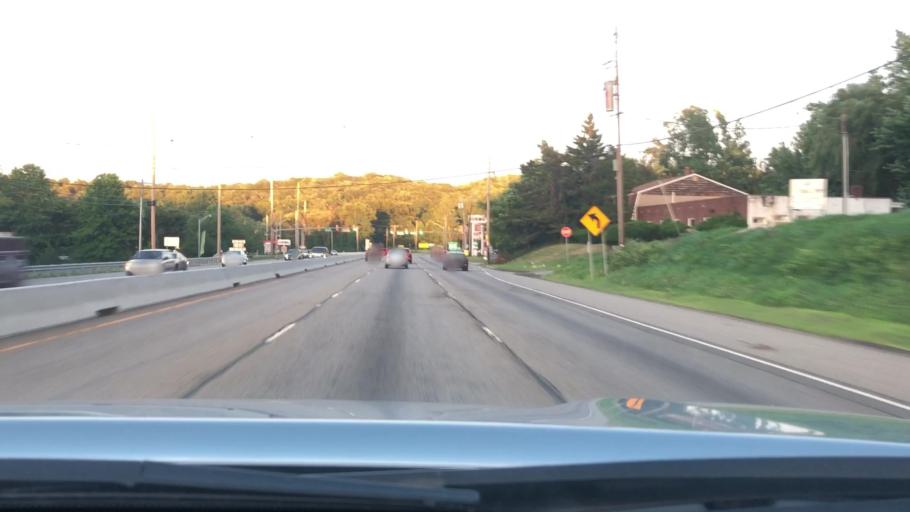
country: US
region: New Jersey
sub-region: Passaic County
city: Bloomingdale
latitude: 40.9883
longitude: -74.3293
